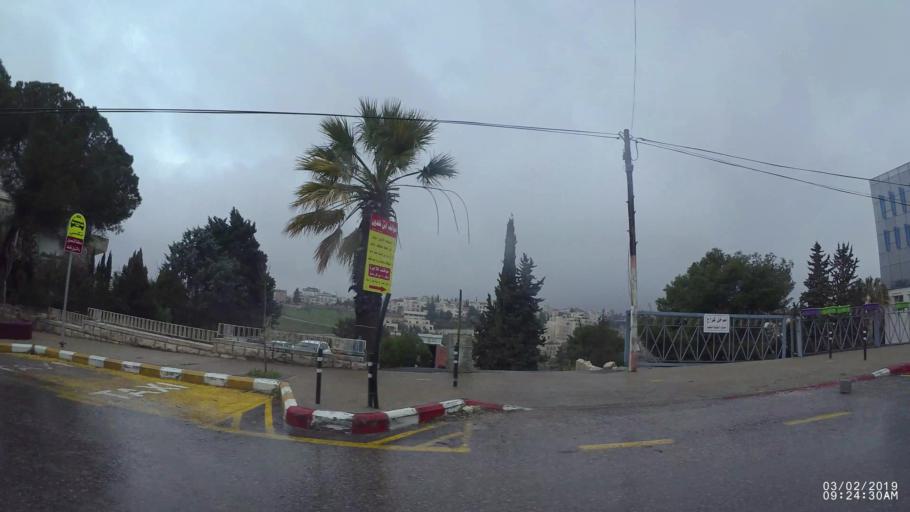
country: JO
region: Amman
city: Amman
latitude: 31.9530
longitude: 35.8996
